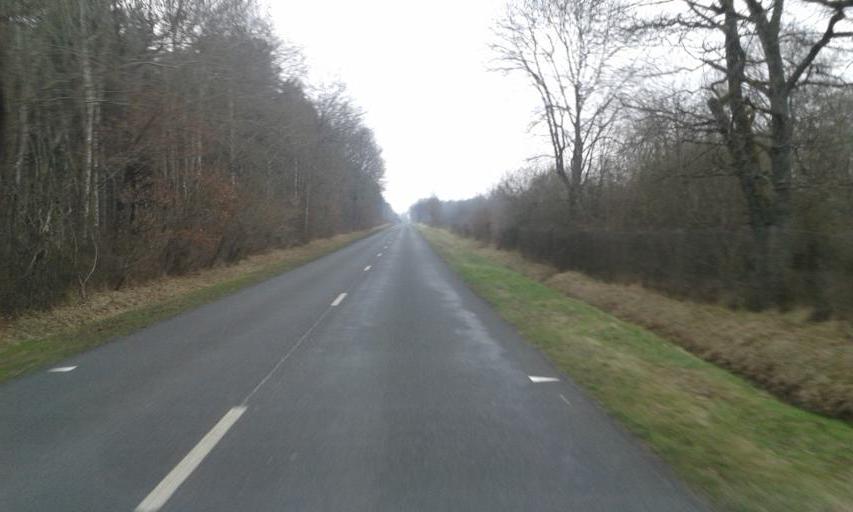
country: FR
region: Centre
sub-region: Departement du Loir-et-Cher
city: Saint-Laurent-Nouan
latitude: 47.6845
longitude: 1.6678
